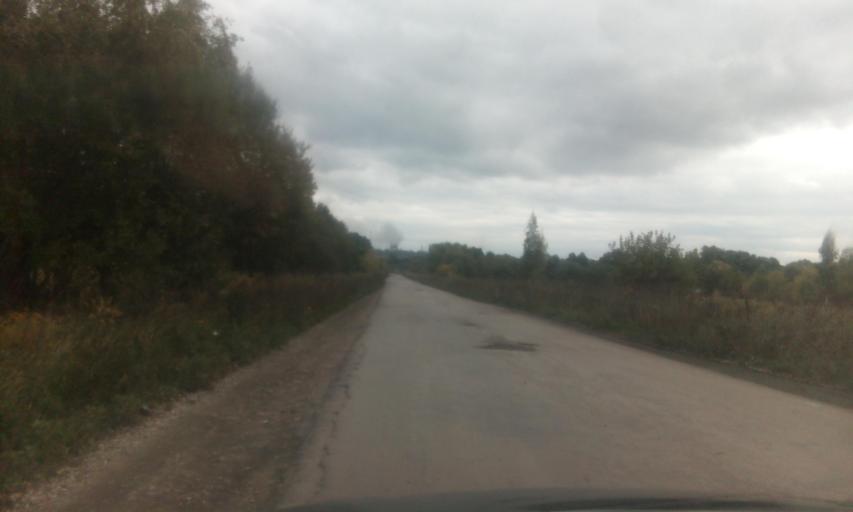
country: RU
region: Tula
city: Gritsovskiy
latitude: 54.1259
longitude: 38.1679
